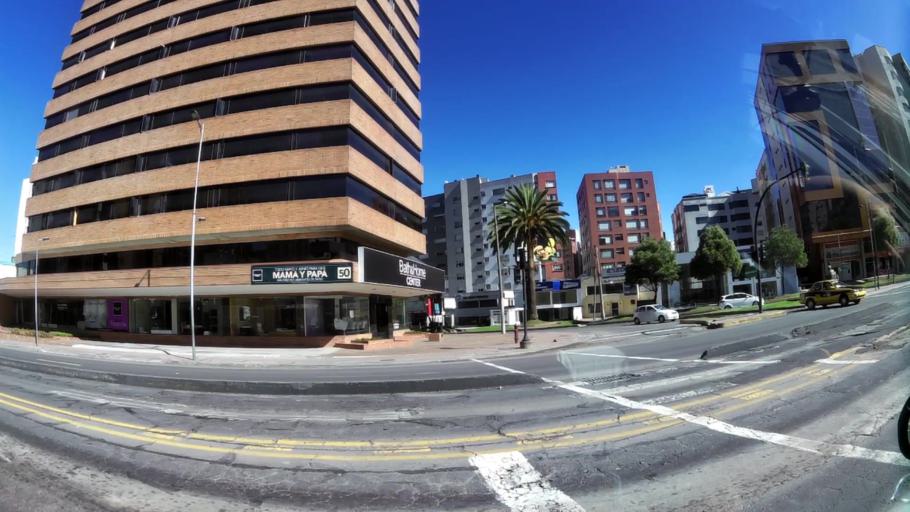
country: EC
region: Pichincha
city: Quito
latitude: -0.1874
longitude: -78.4798
